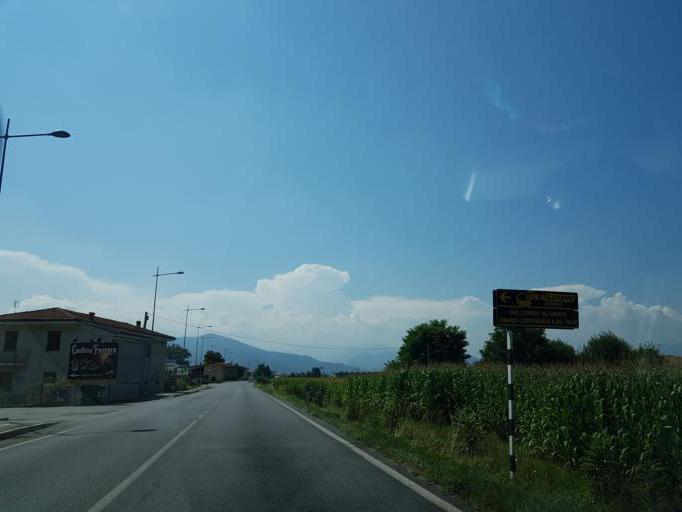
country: IT
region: Piedmont
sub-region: Provincia di Cuneo
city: San Defendente
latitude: 44.3949
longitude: 7.5035
